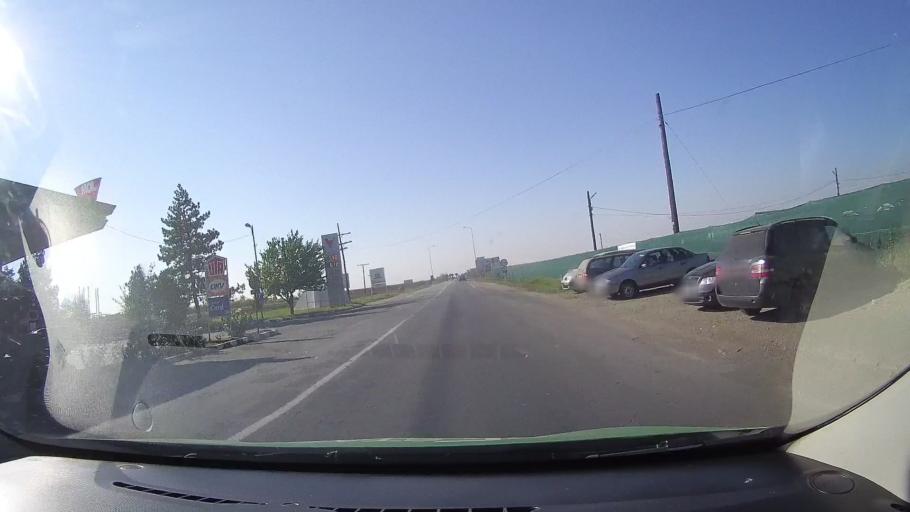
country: RO
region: Satu Mare
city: Carei
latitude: 47.6739
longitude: 22.4446
